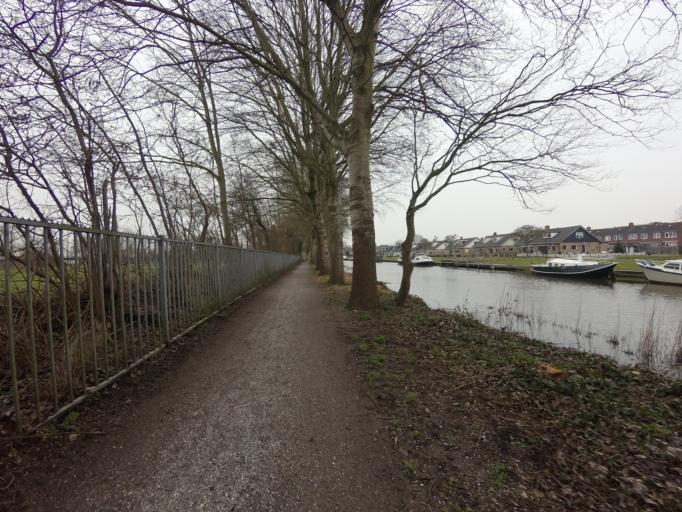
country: NL
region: Friesland
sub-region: Gemeente Franekeradeel
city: Franeker
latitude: 53.1924
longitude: 5.5479
